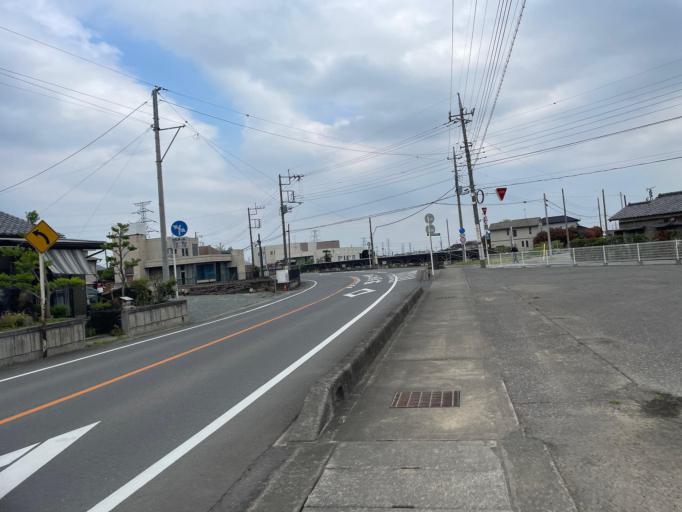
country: JP
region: Gunma
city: Isesaki
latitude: 36.2798
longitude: 139.2048
